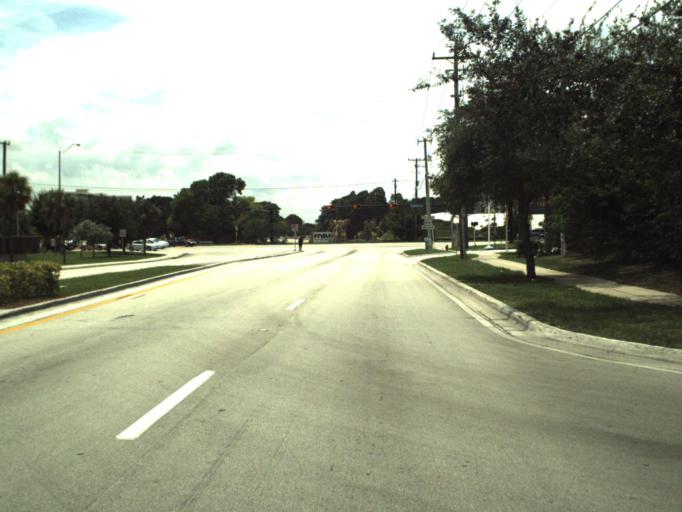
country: US
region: Florida
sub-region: Broward County
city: Coconut Creek
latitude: 26.2327
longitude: -80.1657
